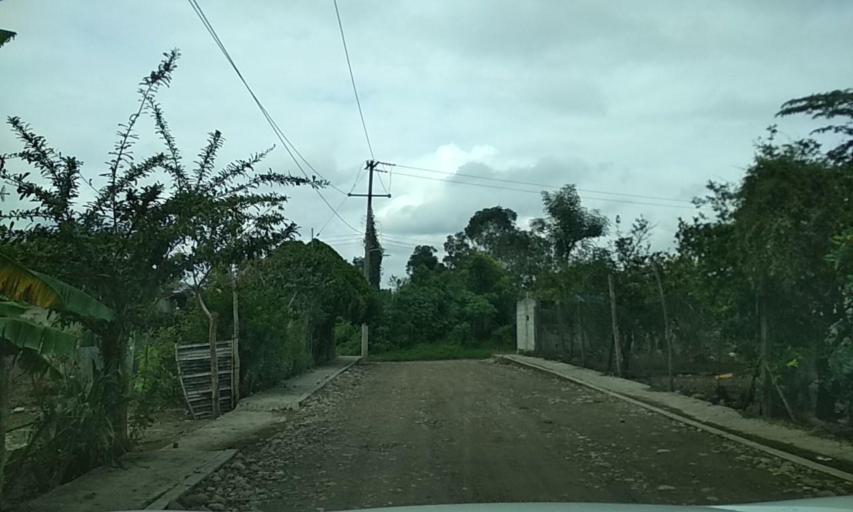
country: MX
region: Veracruz
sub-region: Papantla
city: El Chote
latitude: 20.3653
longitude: -97.4290
